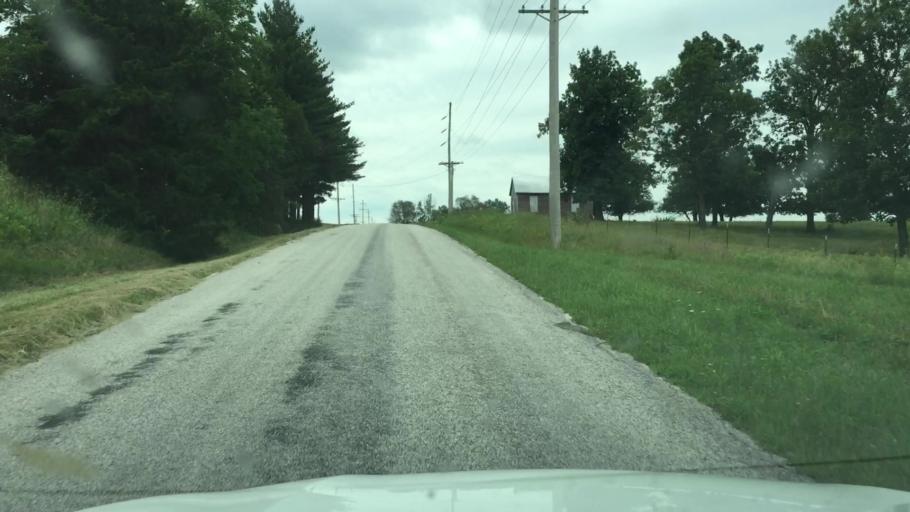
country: US
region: Illinois
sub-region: Hancock County
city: Carthage
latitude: 40.3257
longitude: -91.0826
